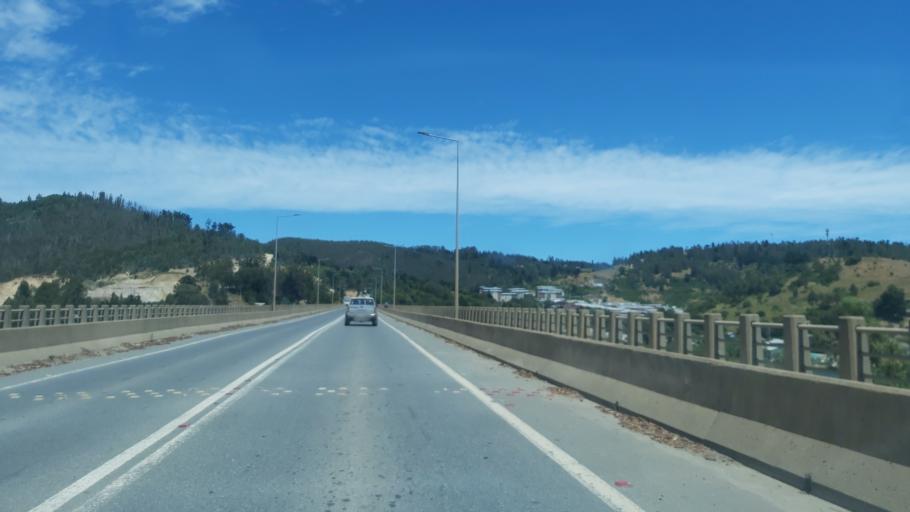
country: CL
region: Maule
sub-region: Provincia de Talca
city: Constitucion
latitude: -35.3398
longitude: -72.3919
